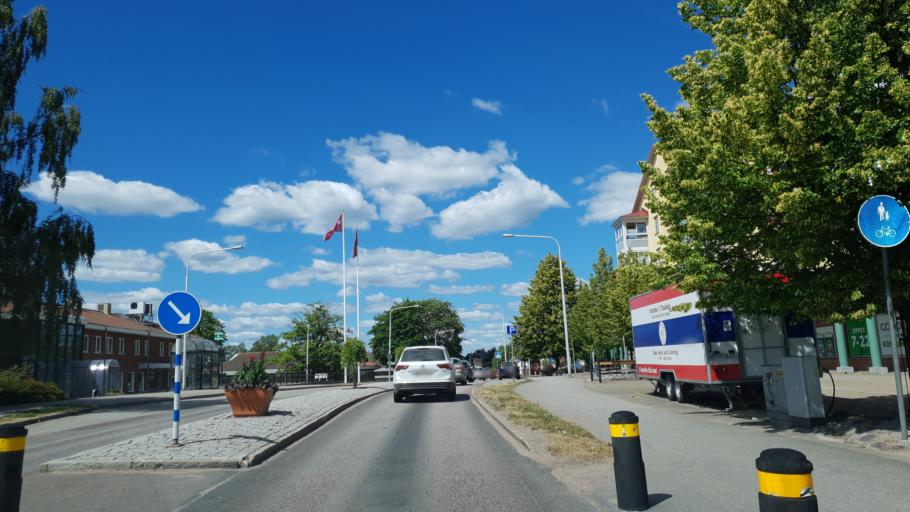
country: SE
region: Kronoberg
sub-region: Lessebo Kommun
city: Lessebo
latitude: 56.7510
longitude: 15.2702
